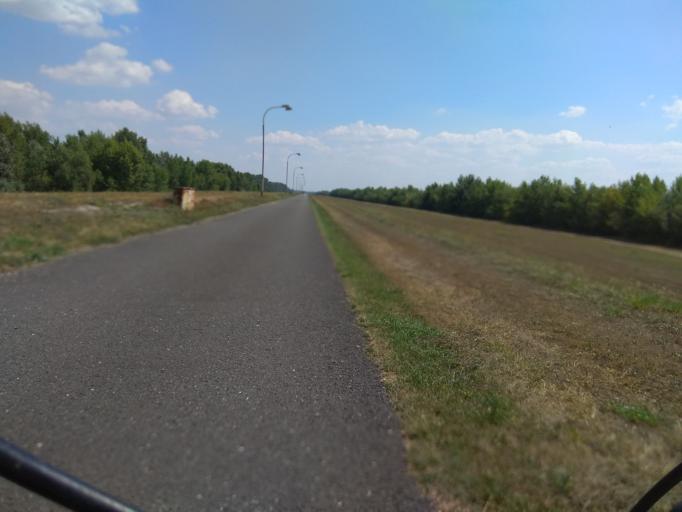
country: SK
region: Trnavsky
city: Gabcikovo
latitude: 47.8613
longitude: 17.5640
